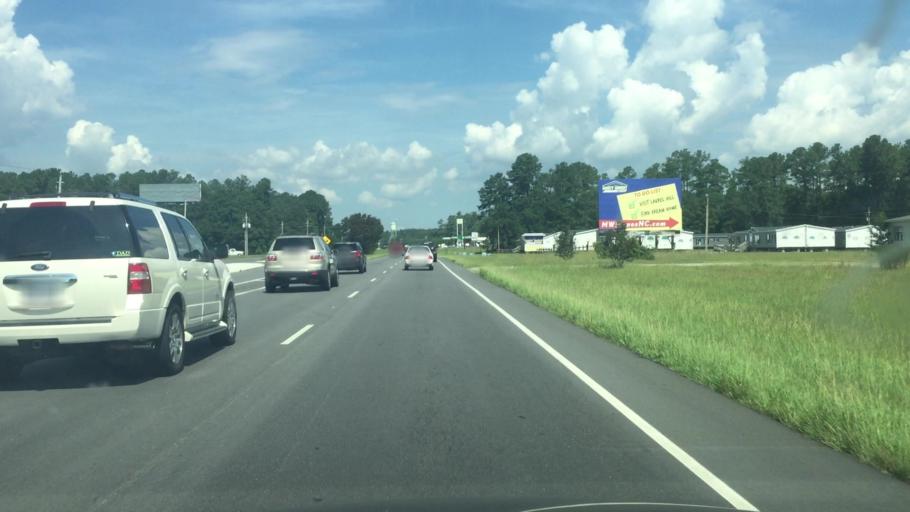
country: US
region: North Carolina
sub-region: Scotland County
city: Laurel Hill
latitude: 34.8031
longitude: -79.5386
